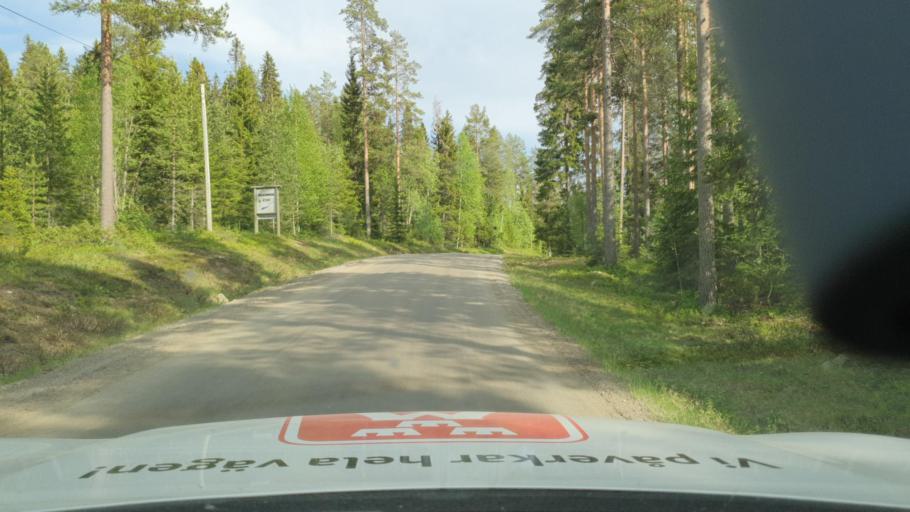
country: SE
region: Vaesterbotten
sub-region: Vindelns Kommun
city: Vindeln
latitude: 64.0971
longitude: 19.6895
